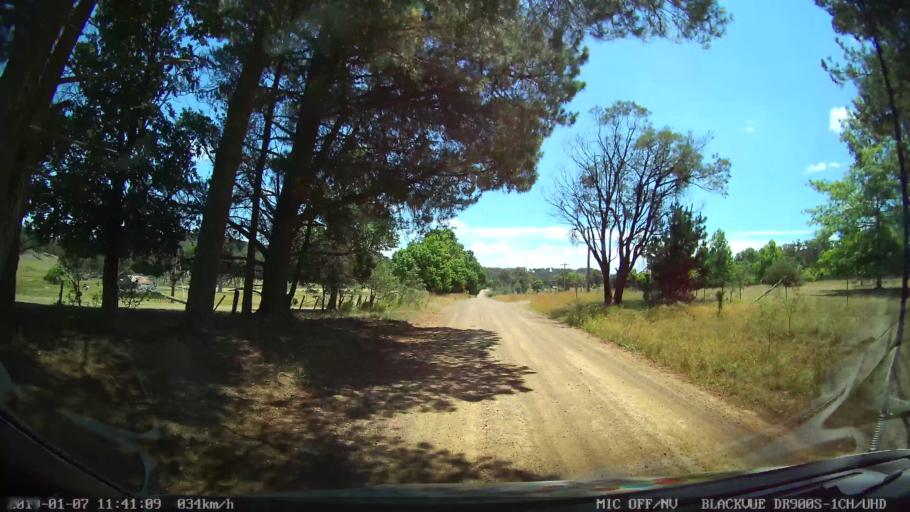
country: AU
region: New South Wales
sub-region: Armidale Dumaresq
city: Armidale
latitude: -30.3617
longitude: 151.5877
